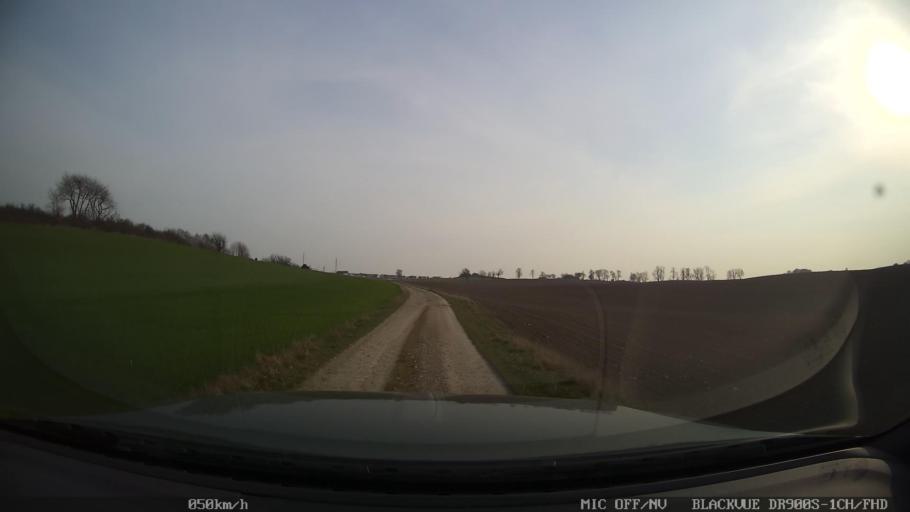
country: SE
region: Skane
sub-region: Ystads Kommun
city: Ystad
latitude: 55.4543
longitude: 13.7931
